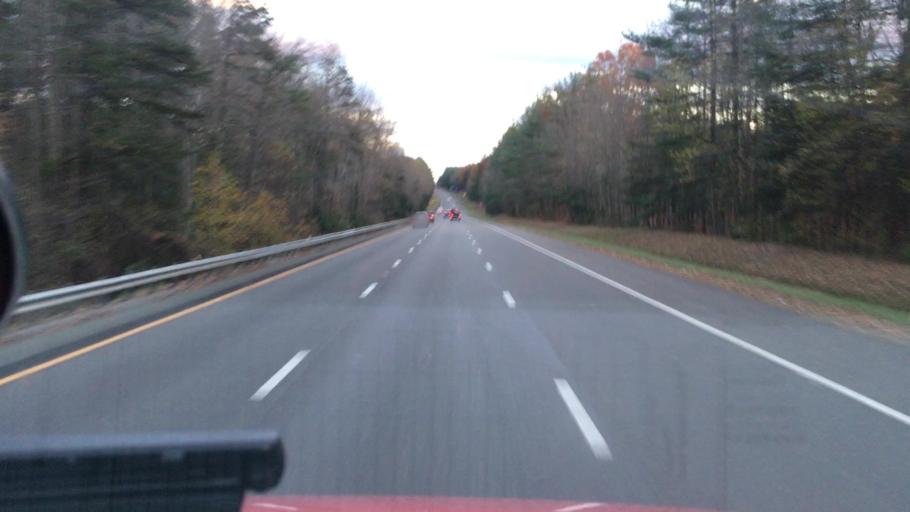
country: US
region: Virginia
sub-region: Fluvanna County
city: Palmyra
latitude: 37.9741
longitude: -78.2073
